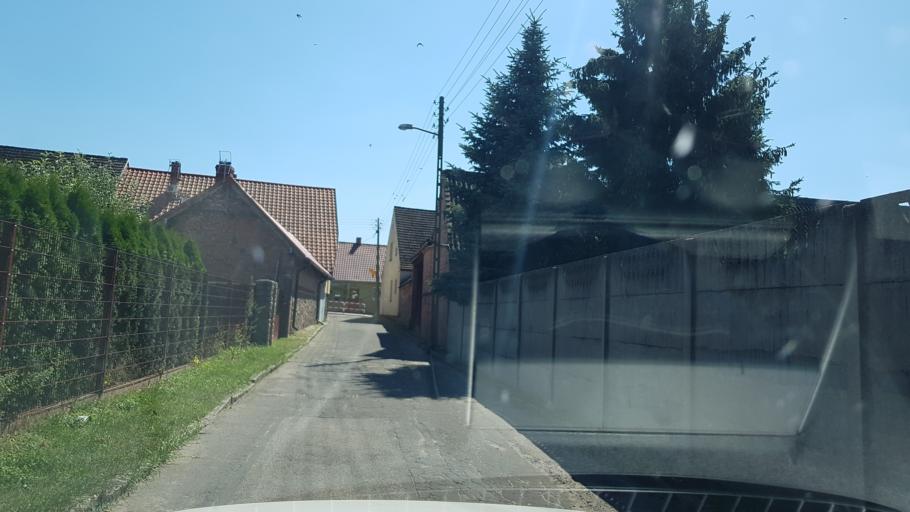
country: PL
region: West Pomeranian Voivodeship
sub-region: Powiat gryfinski
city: Moryn
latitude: 52.8589
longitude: 14.3960
